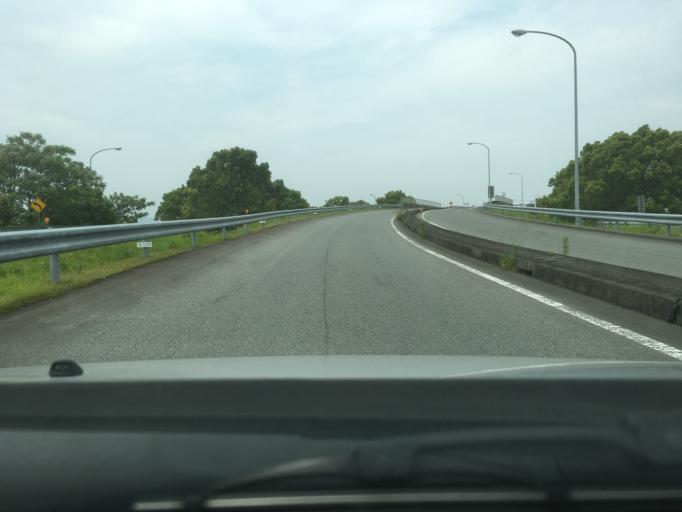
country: JP
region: Kumamoto
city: Kumamoto
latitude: 32.7920
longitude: 130.7867
